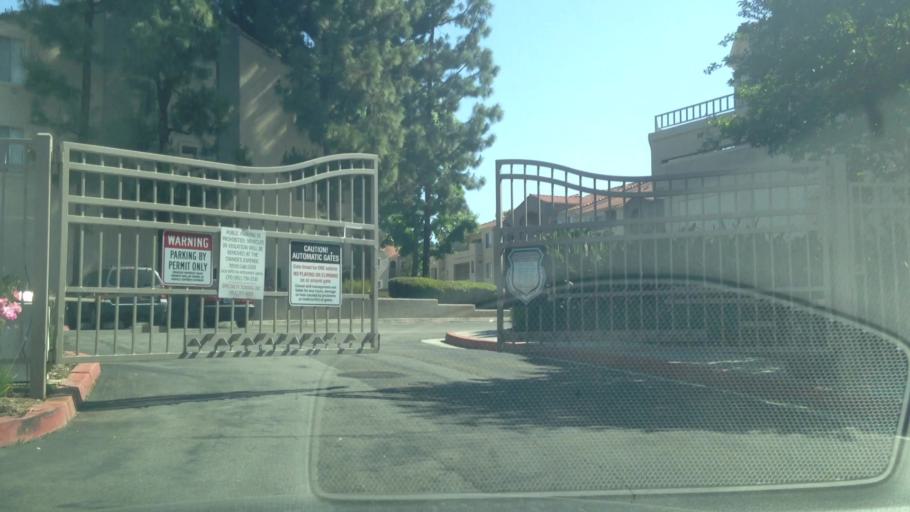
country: US
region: California
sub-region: Riverside County
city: Home Gardens
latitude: 33.8986
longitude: -117.5322
